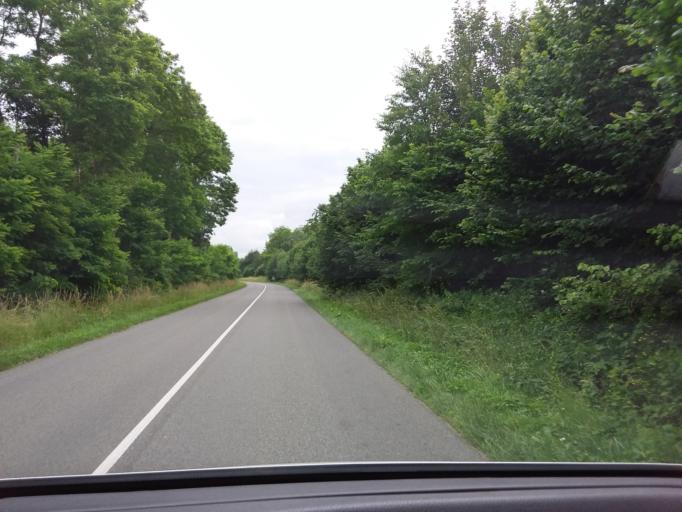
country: FR
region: Picardie
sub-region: Departement de l'Aisne
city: Vailly-sur-Aisne
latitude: 49.4021
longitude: 3.5798
